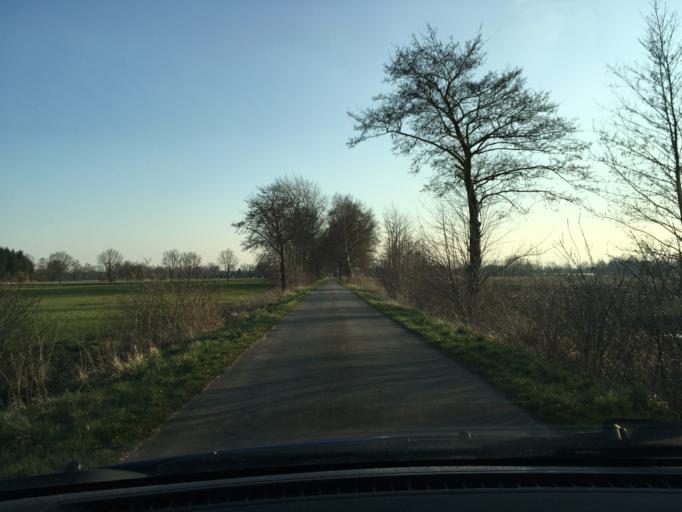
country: DE
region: Lower Saxony
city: Hittbergen
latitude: 53.3181
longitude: 10.6252
